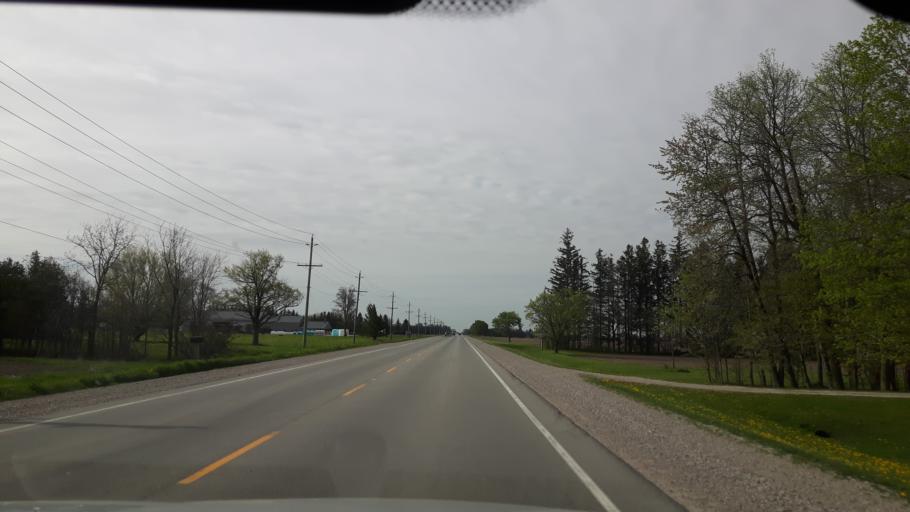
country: CA
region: Ontario
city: South Huron
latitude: 43.4053
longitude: -81.4926
